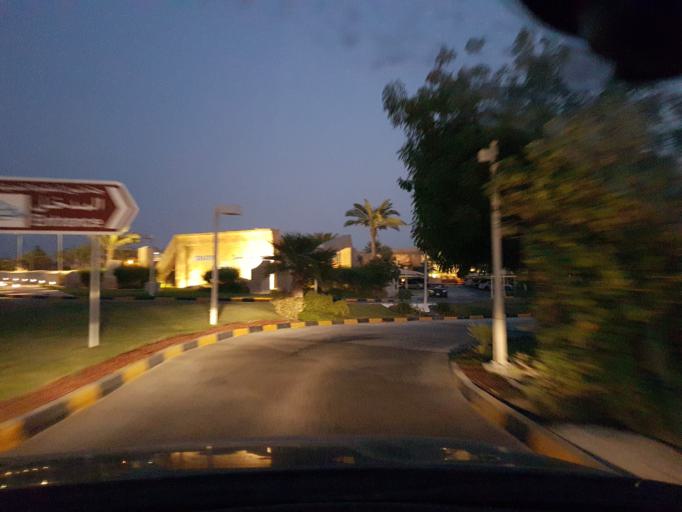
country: BH
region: Central Governorate
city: Dar Kulayb
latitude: 26.0162
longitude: 50.5092
